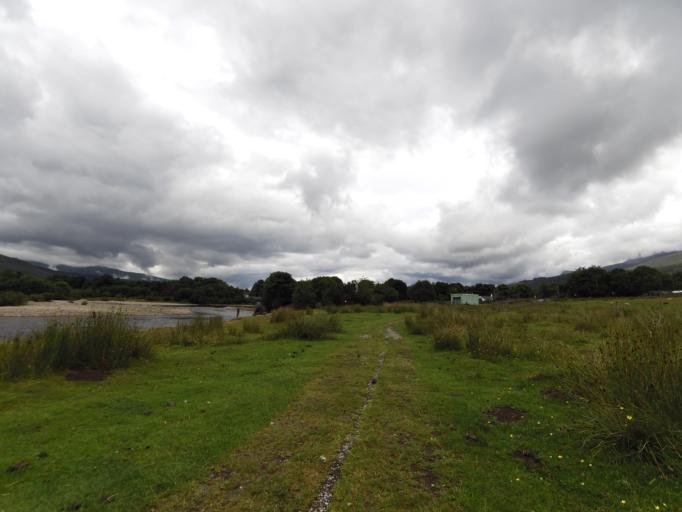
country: GB
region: Scotland
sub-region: Highland
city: Fort William
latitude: 56.8312
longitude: -5.0865
